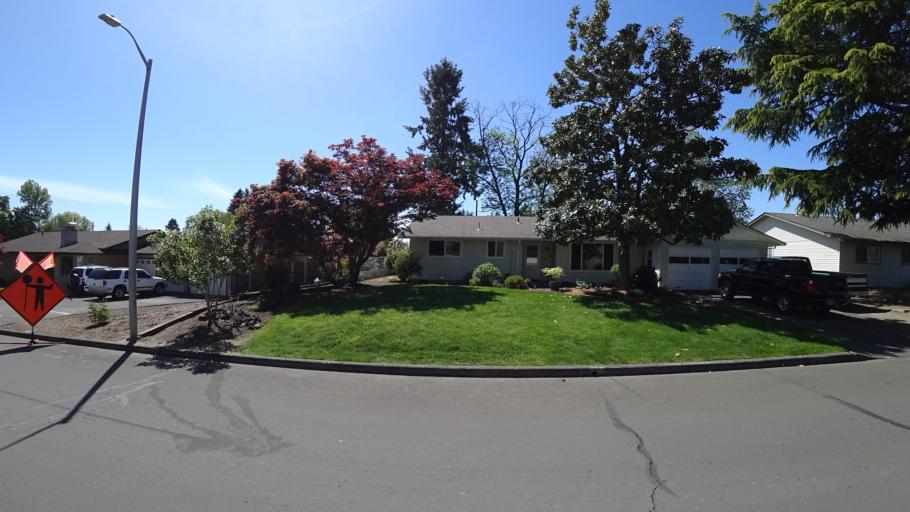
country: US
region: Oregon
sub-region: Washington County
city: Hillsboro
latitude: 45.5113
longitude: -122.9583
